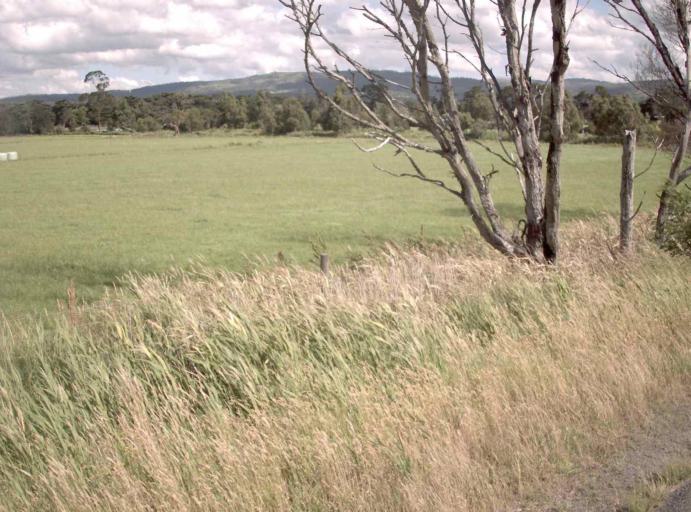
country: AU
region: Victoria
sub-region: Latrobe
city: Morwell
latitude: -38.2876
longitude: 146.4302
